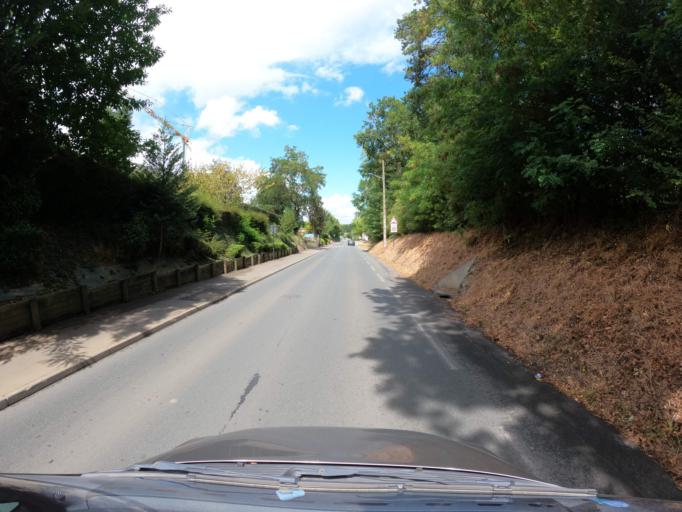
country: FR
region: Pays de la Loire
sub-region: Departement de Maine-et-Loire
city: Feneu
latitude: 47.5325
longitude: -0.6149
